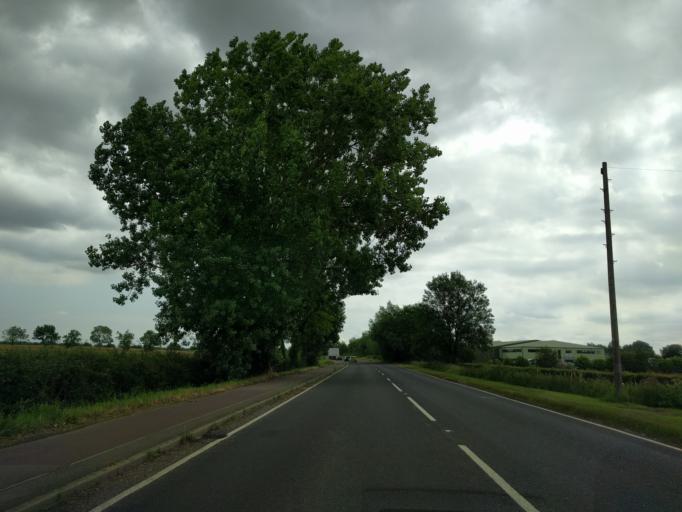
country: GB
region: England
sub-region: Cambridgeshire
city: Needingworth
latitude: 52.3314
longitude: -0.0560
